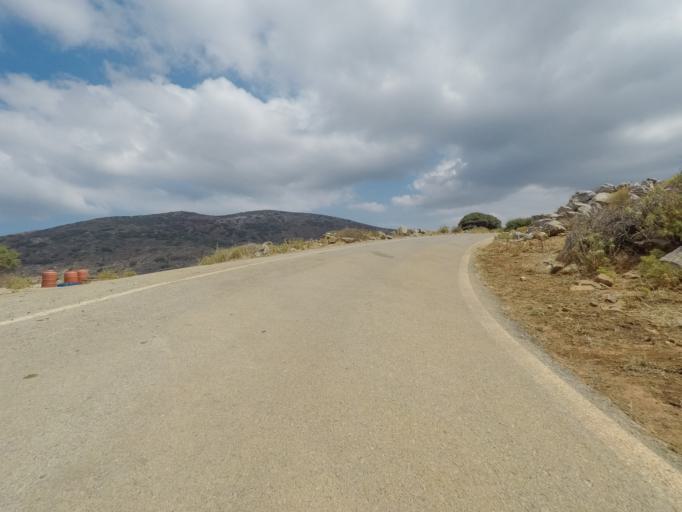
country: GR
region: Crete
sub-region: Nomos Lasithiou
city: Elounda
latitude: 35.3066
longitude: 25.6817
